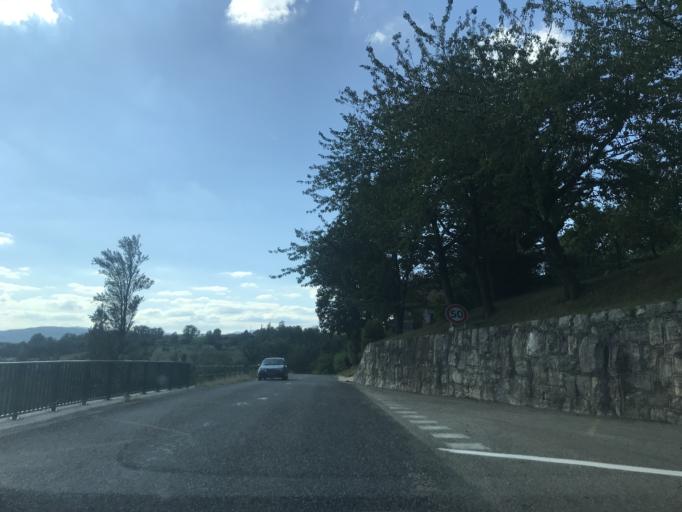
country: FR
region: Rhone-Alpes
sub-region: Departement de la Savoie
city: Yenne
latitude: 45.7157
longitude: 5.8212
